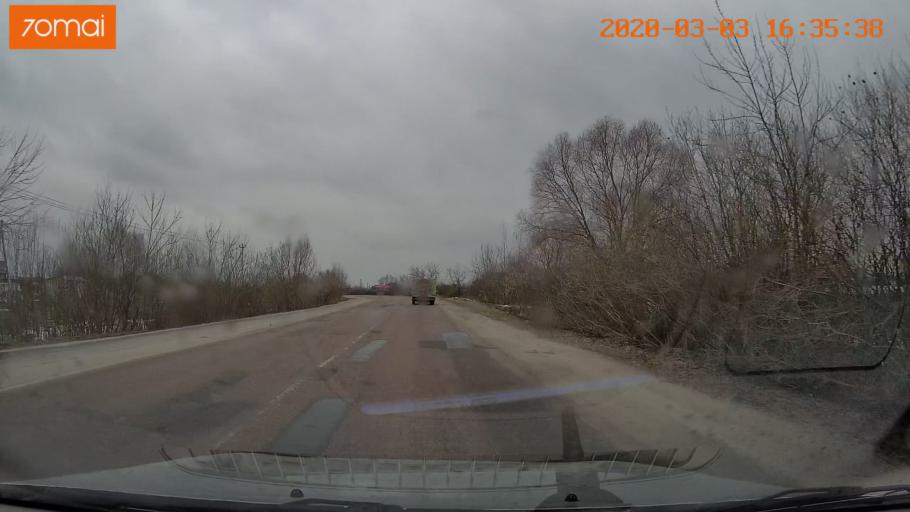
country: RU
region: Moskovskaya
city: Lopatinskiy
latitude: 55.4032
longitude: 38.7652
